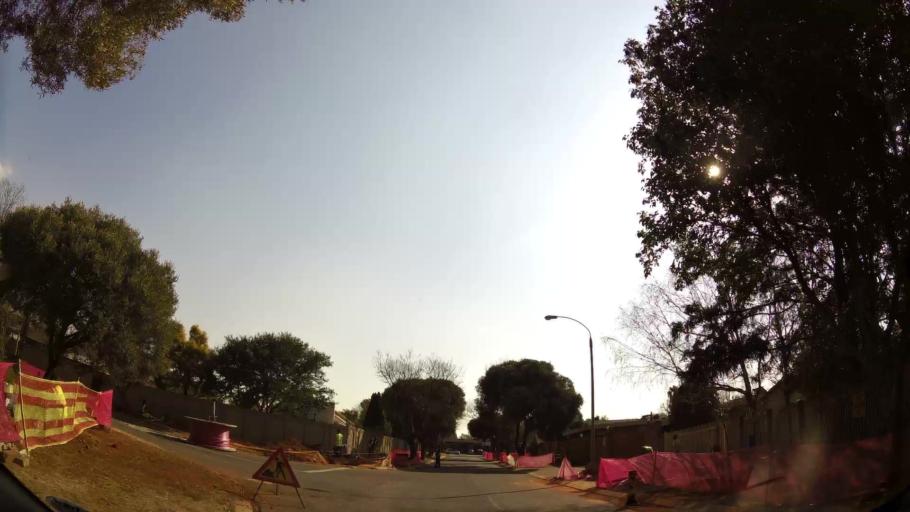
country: ZA
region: Gauteng
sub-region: Ekurhuleni Metropolitan Municipality
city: Benoni
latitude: -26.1550
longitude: 28.2841
